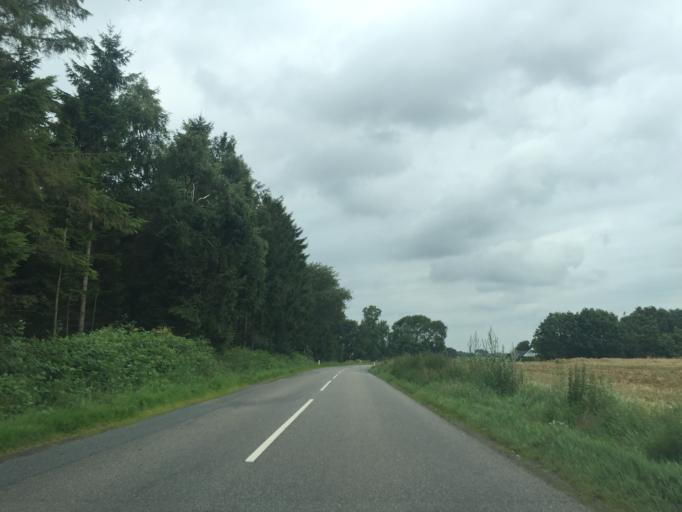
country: DK
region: Central Jutland
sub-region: Favrskov Kommune
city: Ulstrup
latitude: 56.3038
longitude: 9.7682
